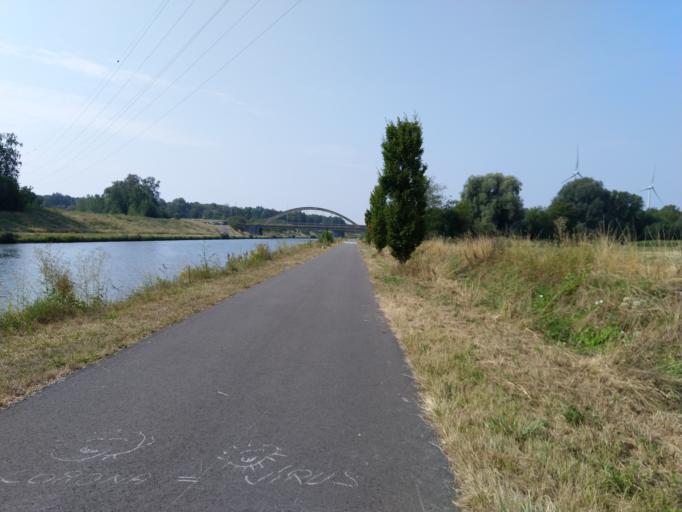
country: BE
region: Wallonia
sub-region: Province du Hainaut
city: La Louviere
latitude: 50.5049
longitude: 4.2038
